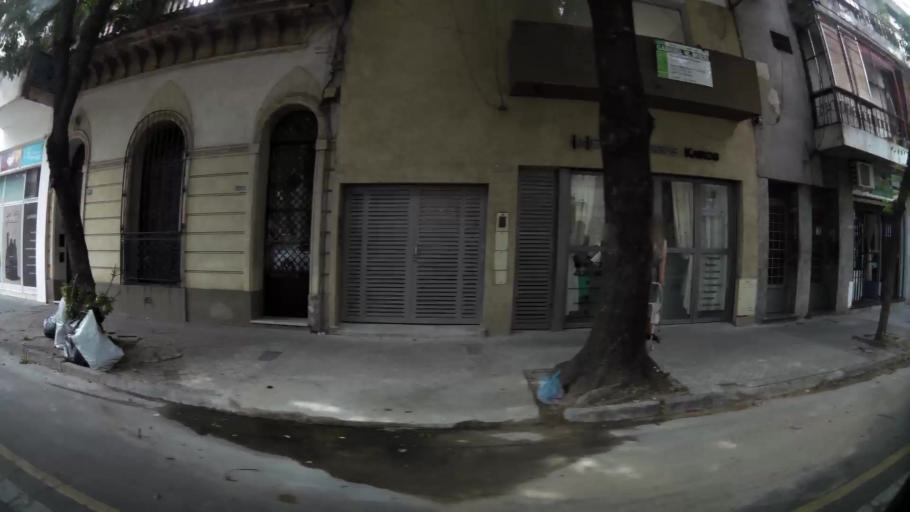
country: AR
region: Santa Fe
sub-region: Departamento de Rosario
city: Rosario
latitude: -32.9663
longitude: -60.6328
